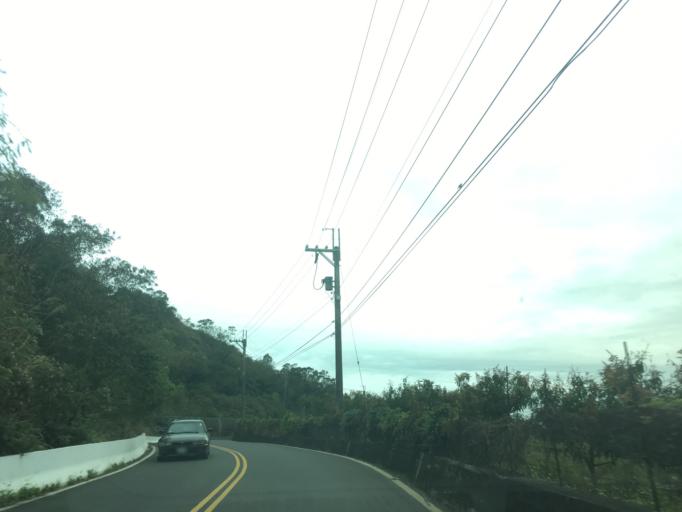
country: TW
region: Taiwan
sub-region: Taitung
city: Taitung
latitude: 22.8149
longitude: 121.1383
